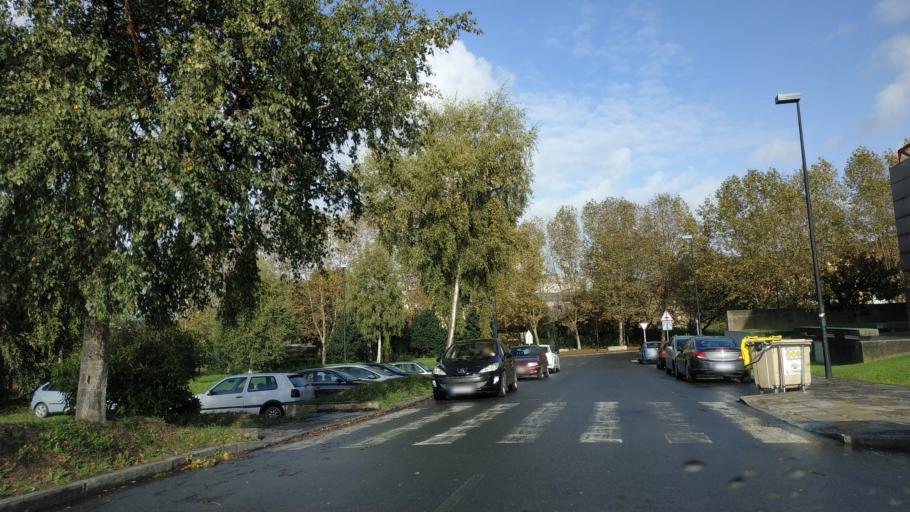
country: ES
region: Galicia
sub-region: Provincia da Coruna
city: A Coruna
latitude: 43.3341
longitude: -8.4063
